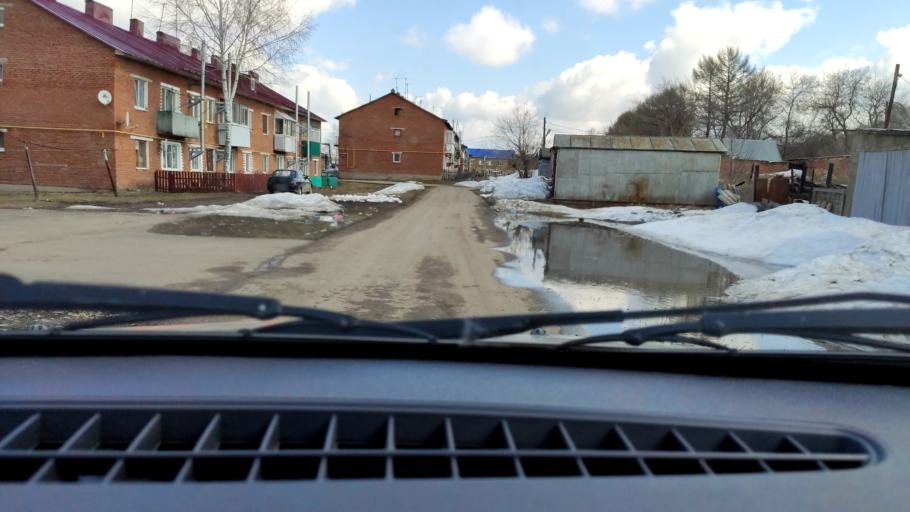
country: RU
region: Bashkortostan
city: Kudeyevskiy
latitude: 54.8672
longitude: 56.7427
